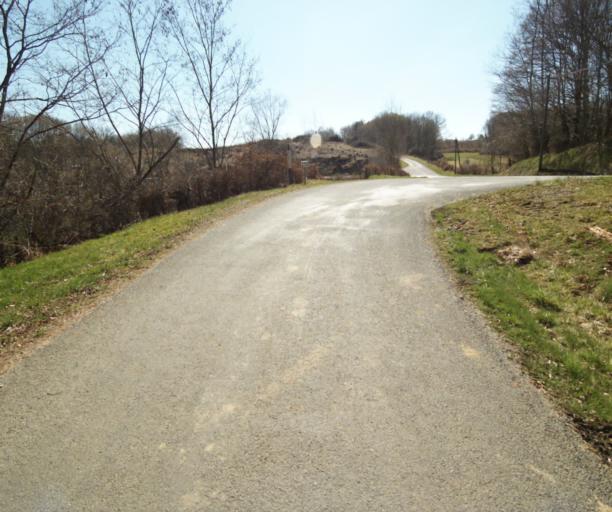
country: FR
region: Limousin
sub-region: Departement de la Correze
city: Saint-Clement
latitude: 45.3180
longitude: 1.6959
